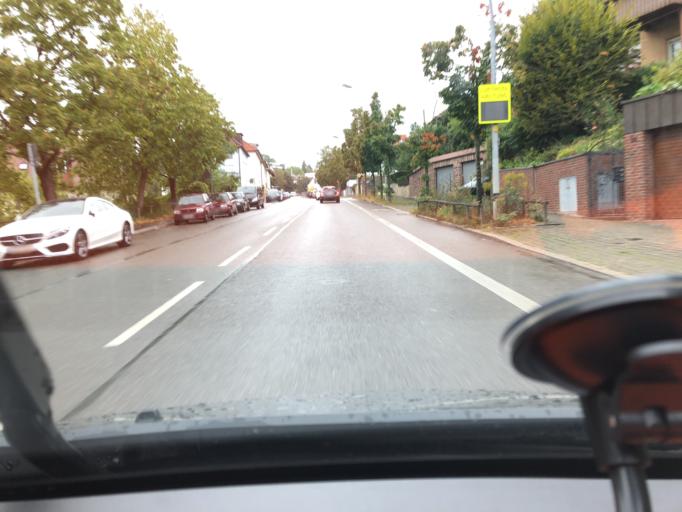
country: DE
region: Baden-Wuerttemberg
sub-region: Regierungsbezirk Stuttgart
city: Stuttgart-Ost
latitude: 48.7719
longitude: 9.1974
